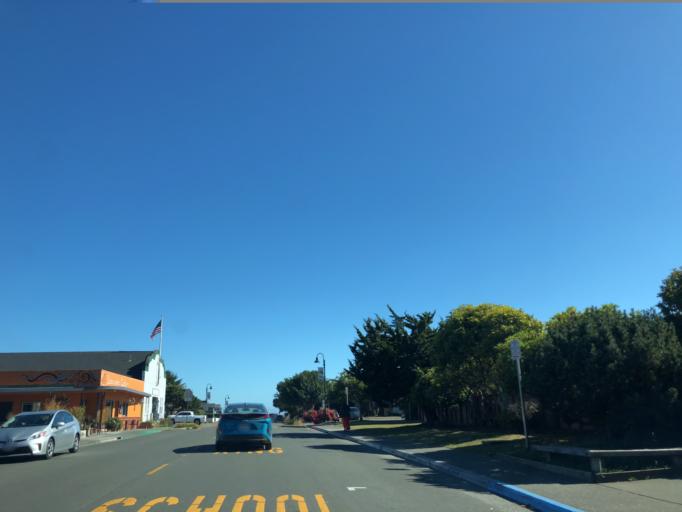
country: US
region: California
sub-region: Humboldt County
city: Westhaven-Moonstone
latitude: 41.0609
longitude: -124.1431
